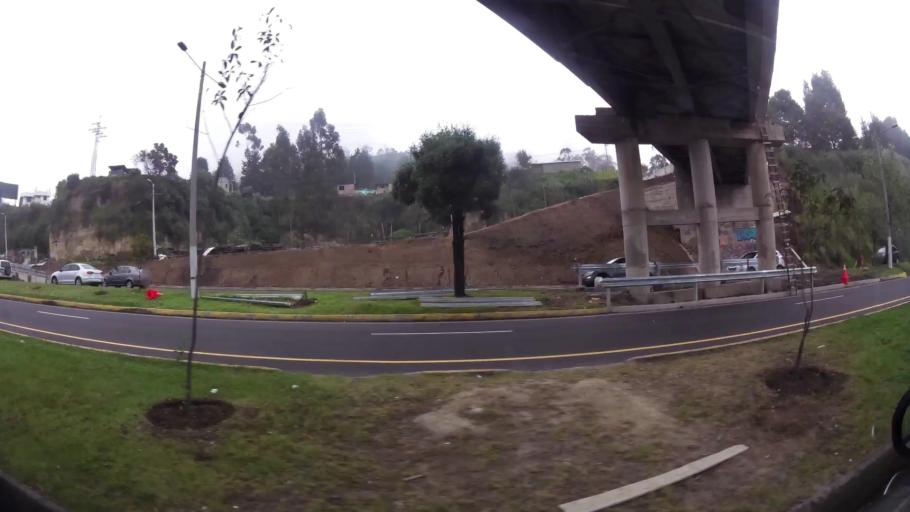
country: EC
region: Pichincha
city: Quito
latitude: -0.2464
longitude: -78.4847
